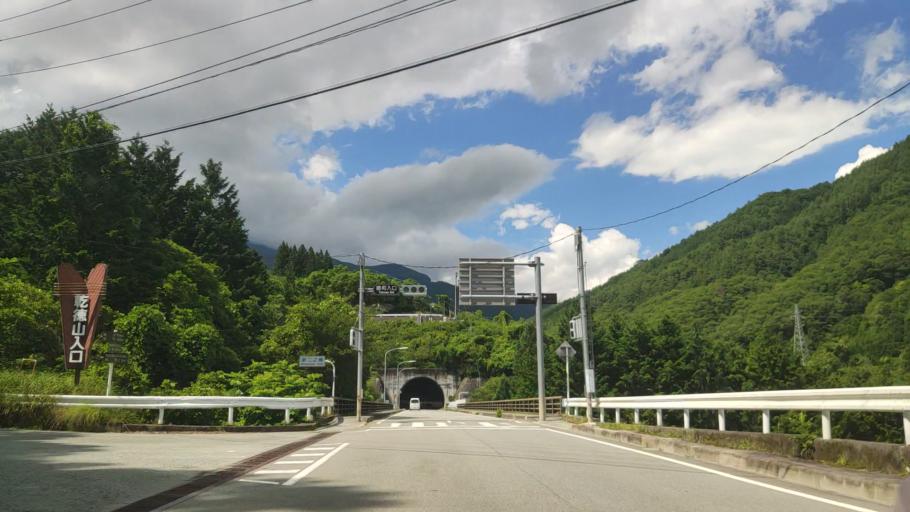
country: JP
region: Yamanashi
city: Enzan
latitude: 35.7778
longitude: 138.7387
